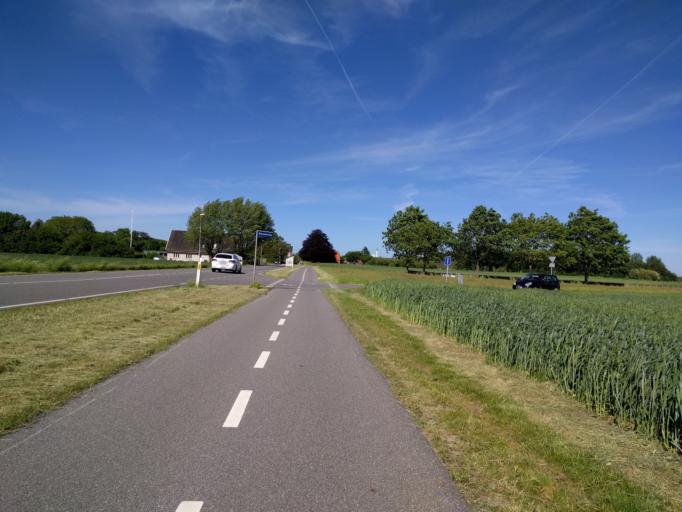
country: DK
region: South Denmark
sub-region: Nyborg Kommune
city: Ullerslev
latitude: 55.4048
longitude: 10.6185
